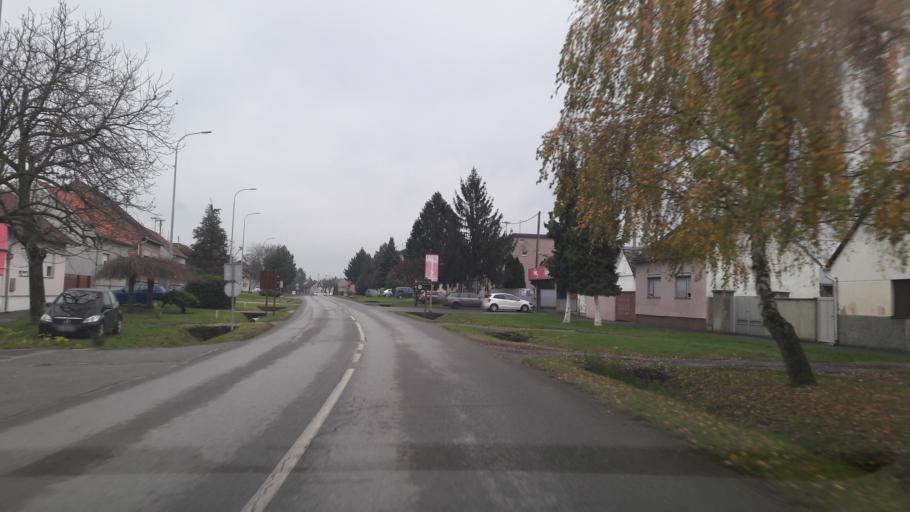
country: HR
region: Osjecko-Baranjska
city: Josipovac
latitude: 45.5781
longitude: 18.5868
